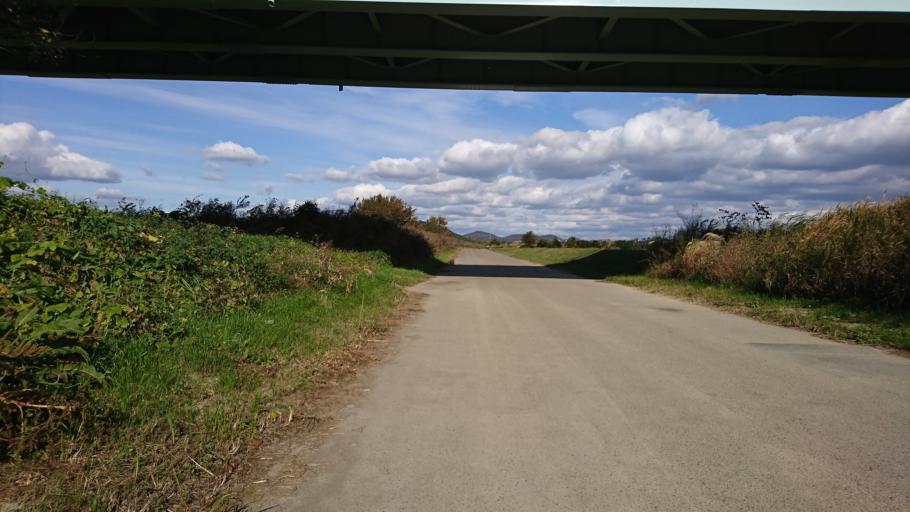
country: JP
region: Hyogo
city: Kakogawacho-honmachi
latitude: 34.7886
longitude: 134.8668
